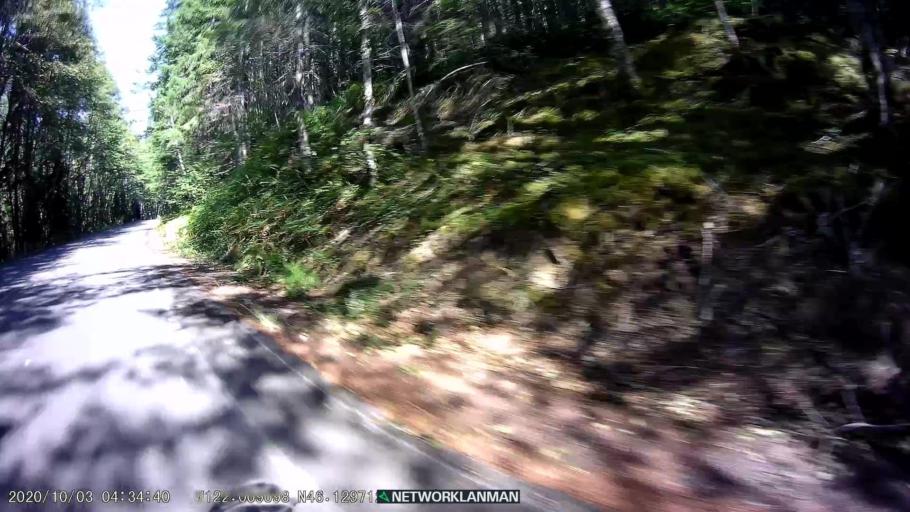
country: US
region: Washington
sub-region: Skamania County
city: Carson
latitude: 46.1300
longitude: -122.0091
